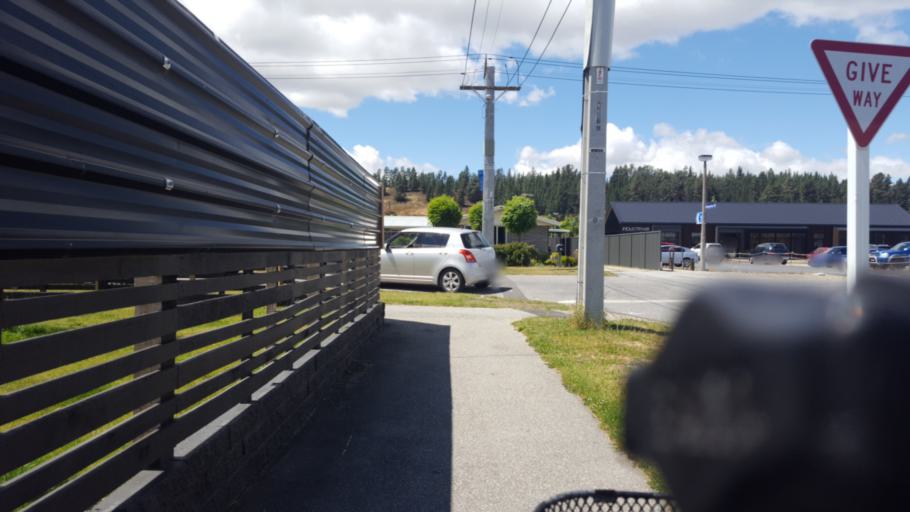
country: NZ
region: Otago
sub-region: Queenstown-Lakes District
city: Wanaka
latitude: -45.2438
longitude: 169.3913
